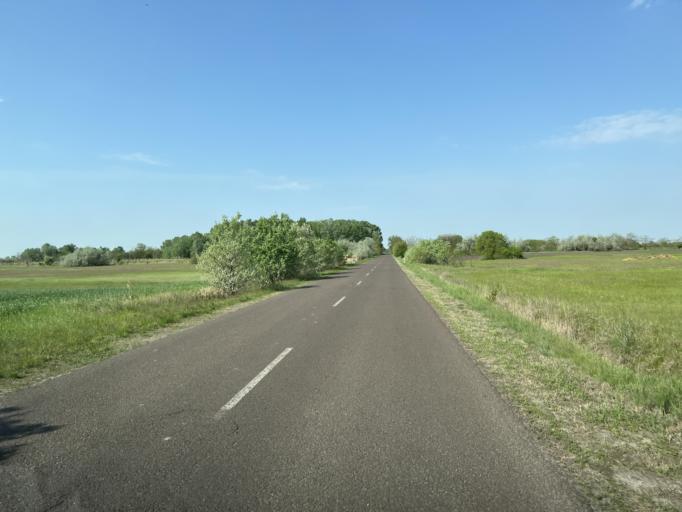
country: HU
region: Pest
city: Jaszkarajeno
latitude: 47.0368
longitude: 20.0431
